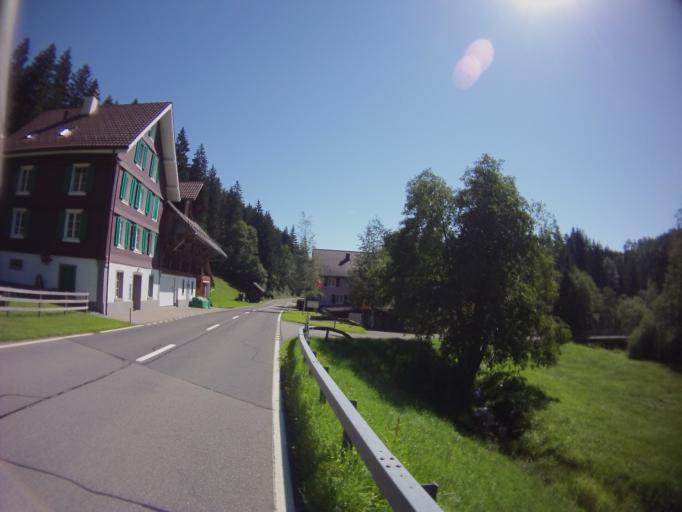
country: CH
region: Schwyz
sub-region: Bezirk Hoefe
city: Schindellegi
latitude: 47.1505
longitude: 8.6968
